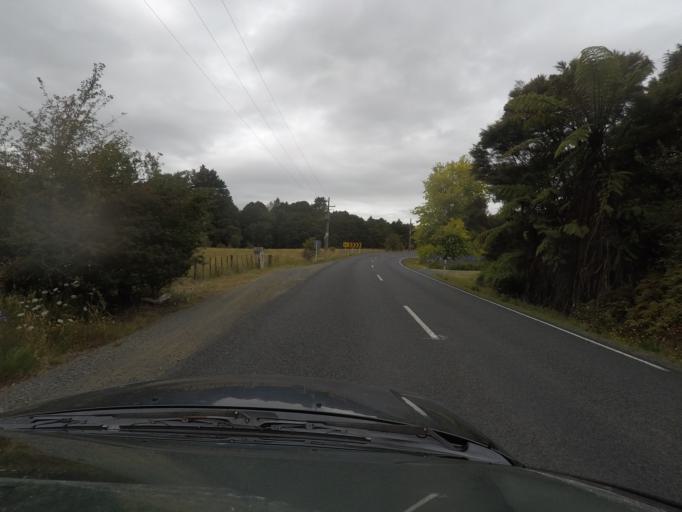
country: NZ
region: Auckland
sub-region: Auckland
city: Wellsford
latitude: -36.2792
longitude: 174.5811
